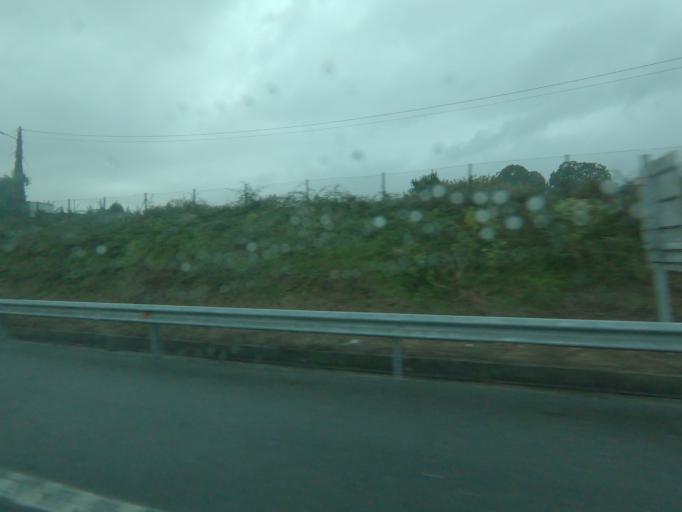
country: ES
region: Galicia
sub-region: Provincia de Pontevedra
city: Poio
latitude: 42.4092
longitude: -8.6535
